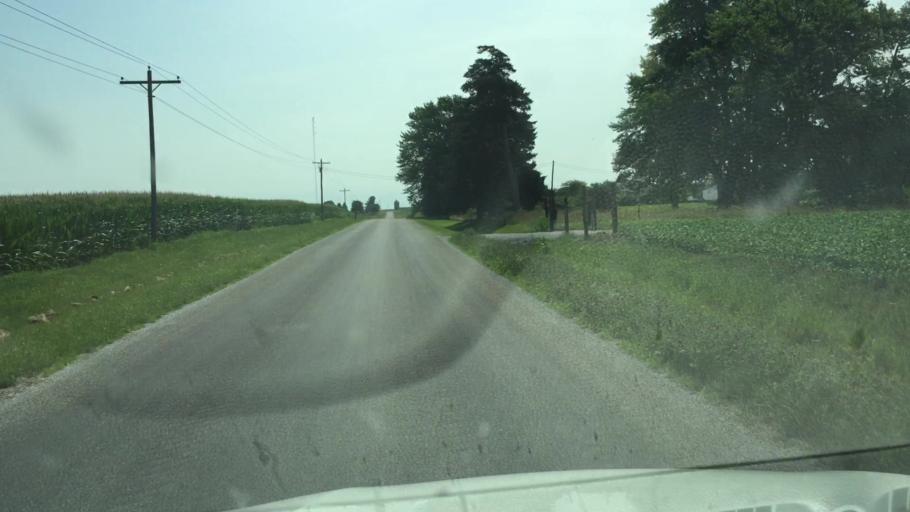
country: US
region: Illinois
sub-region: Hancock County
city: Nauvoo
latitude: 40.5113
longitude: -91.3380
